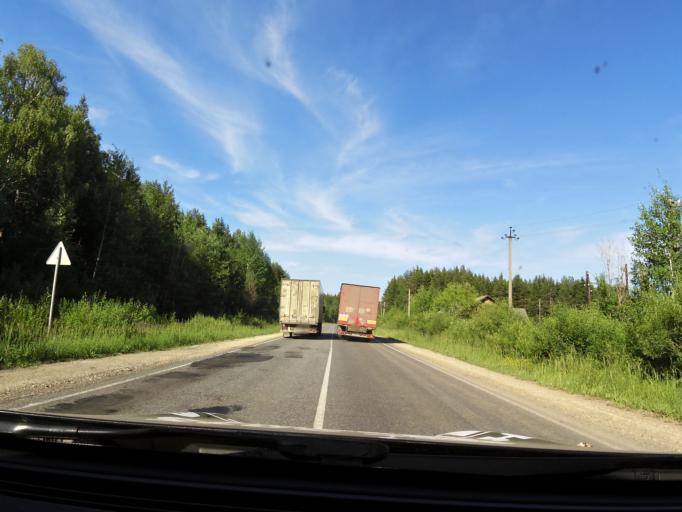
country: RU
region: Kirov
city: Belaya Kholunitsa
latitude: 58.8710
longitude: 50.8469
